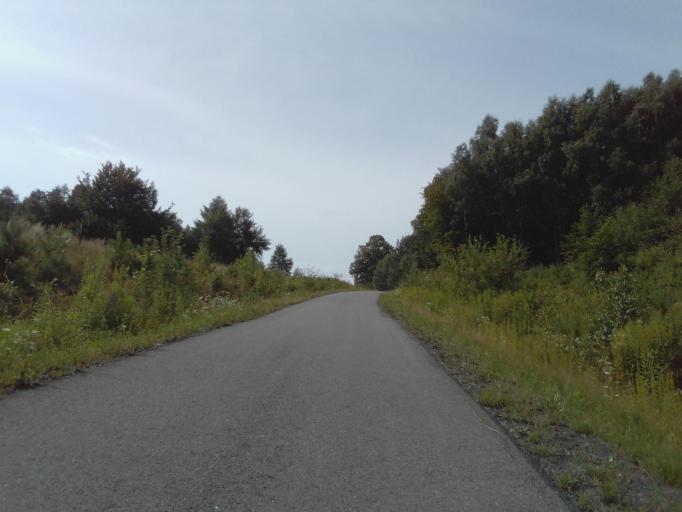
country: PL
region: Subcarpathian Voivodeship
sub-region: Powiat strzyzowski
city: Frysztak
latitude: 49.8697
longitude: 21.5260
